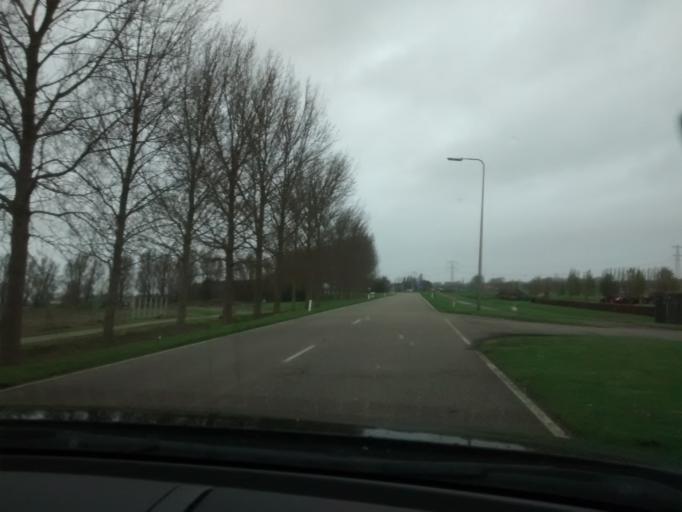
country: NL
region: South Holland
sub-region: Gemeente Spijkenisse
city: Spijkenisse
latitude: 51.8332
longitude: 4.2537
